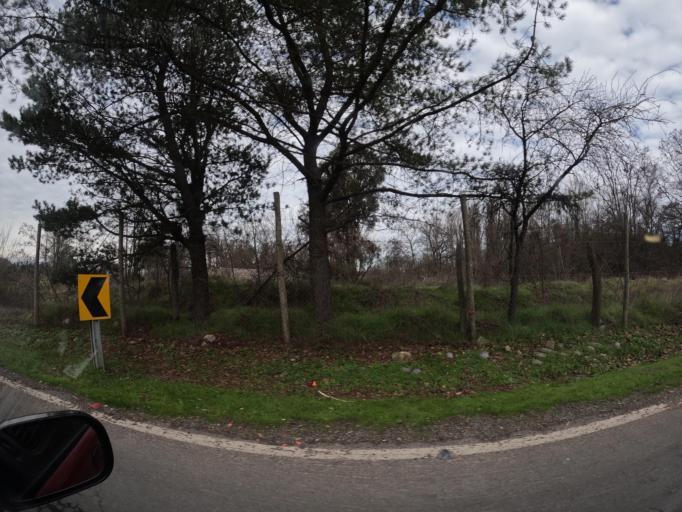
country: CL
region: Maule
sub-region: Provincia de Linares
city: Linares
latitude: -35.8659
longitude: -71.6236
